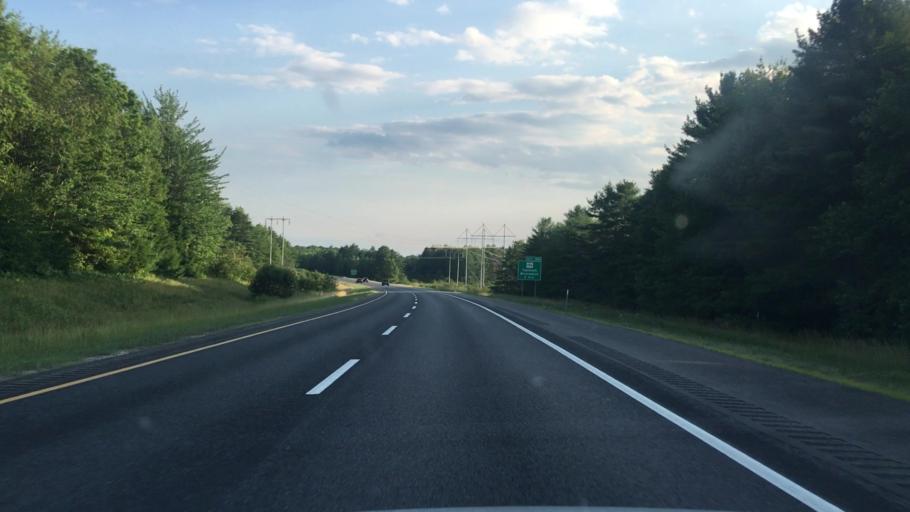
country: US
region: Maine
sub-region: Sagadahoc County
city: Topsham
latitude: 43.9696
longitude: -69.9537
